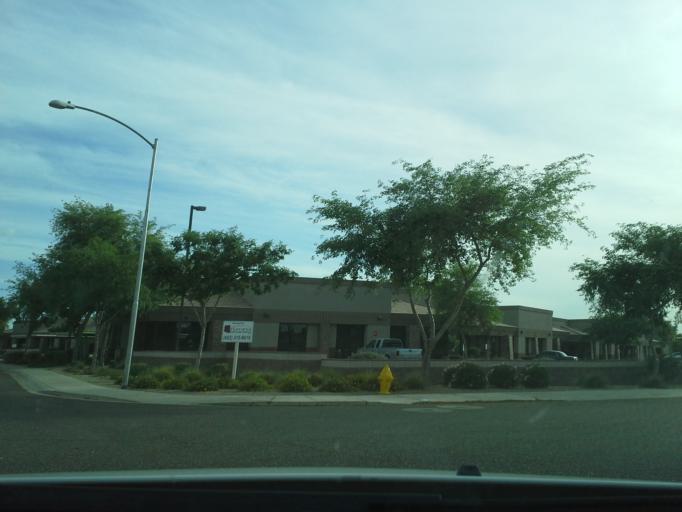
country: US
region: Arizona
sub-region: Maricopa County
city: Peoria
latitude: 33.6427
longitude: -112.2126
